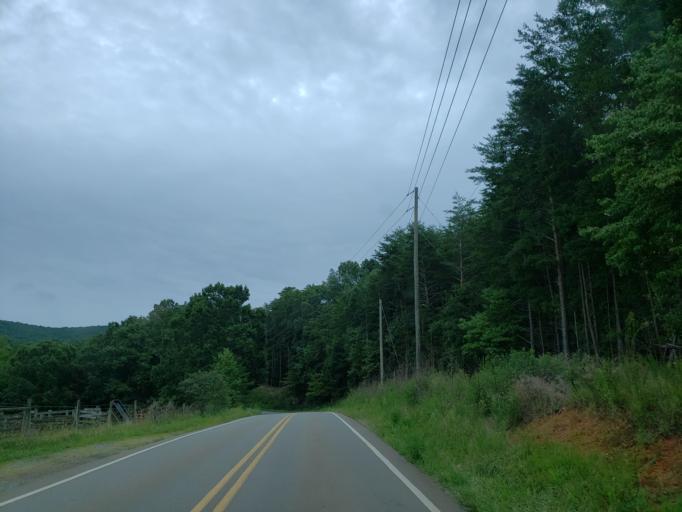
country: US
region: Georgia
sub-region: Pickens County
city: Jasper
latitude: 34.4258
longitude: -84.5449
